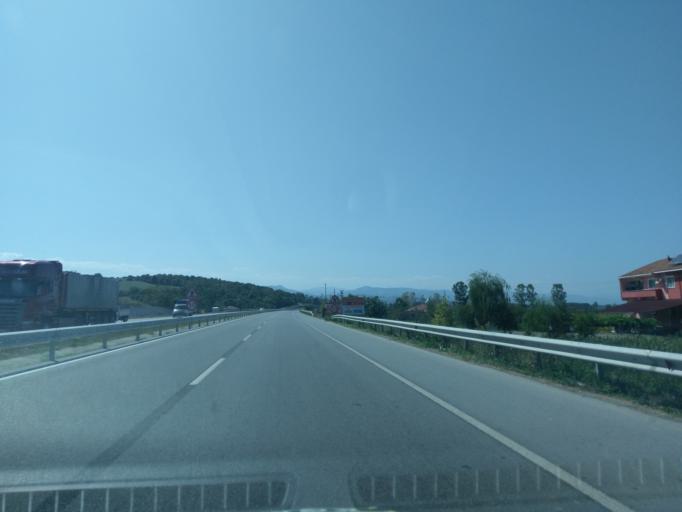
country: TR
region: Samsun
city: Alacam
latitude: 41.6100
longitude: 35.6960
